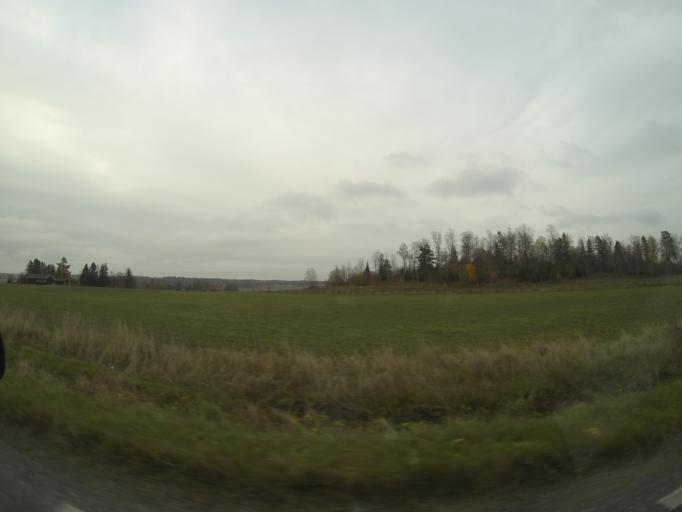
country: SE
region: Vaestmanland
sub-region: Vasteras
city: Skultuna
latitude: 59.6790
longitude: 16.4488
